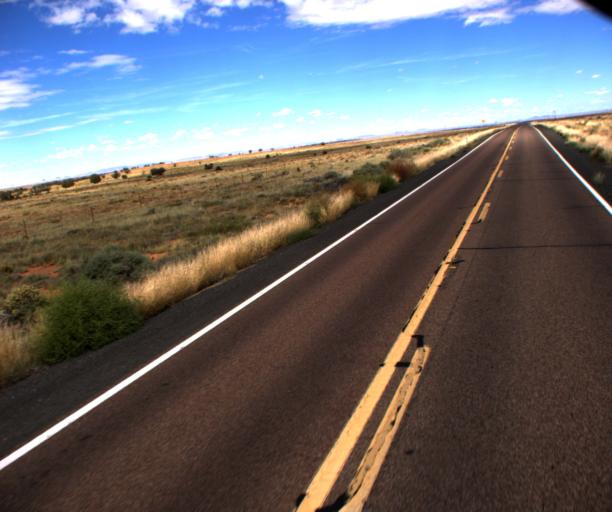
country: US
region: Arizona
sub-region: Navajo County
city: Holbrook
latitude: 34.7655
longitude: -110.2455
